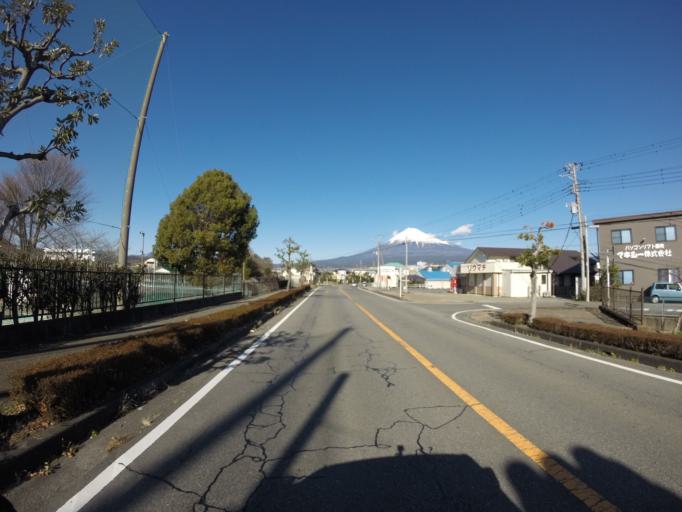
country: JP
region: Shizuoka
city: Fuji
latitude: 35.1682
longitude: 138.6536
